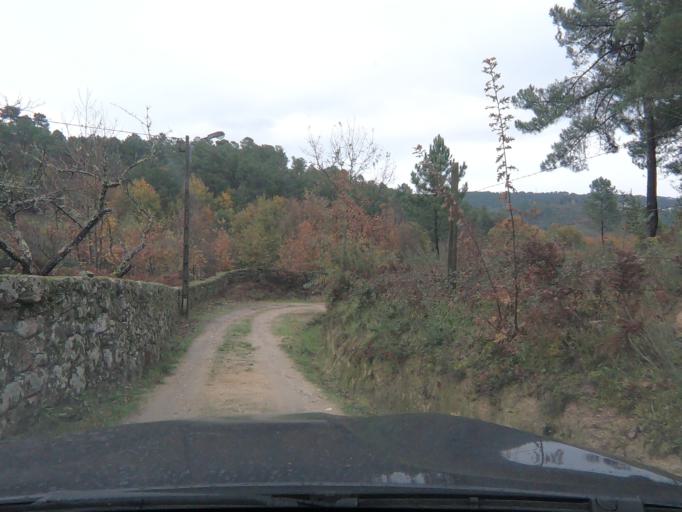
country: PT
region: Vila Real
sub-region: Vila Real
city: Vila Real
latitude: 41.3243
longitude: -7.7277
